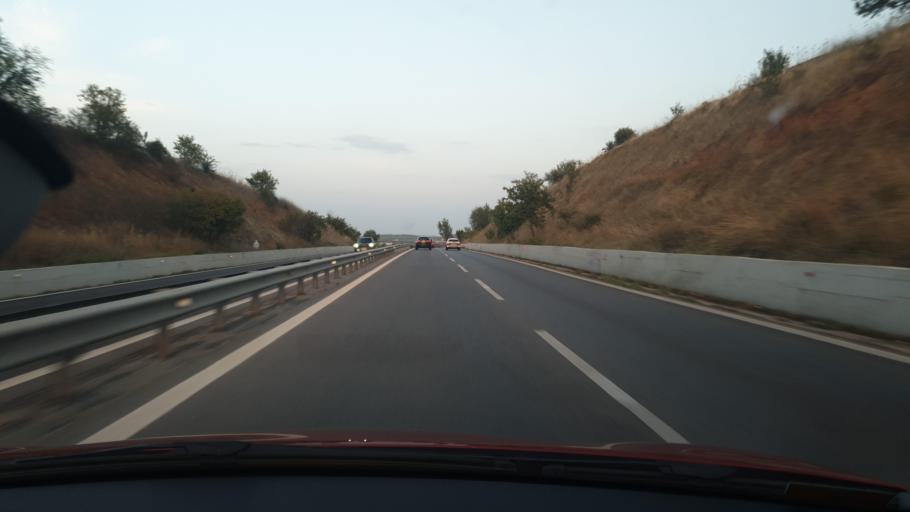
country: GR
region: Central Macedonia
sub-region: Nomos Chalkidikis
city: Nea Flogita
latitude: 40.2640
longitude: 23.2446
